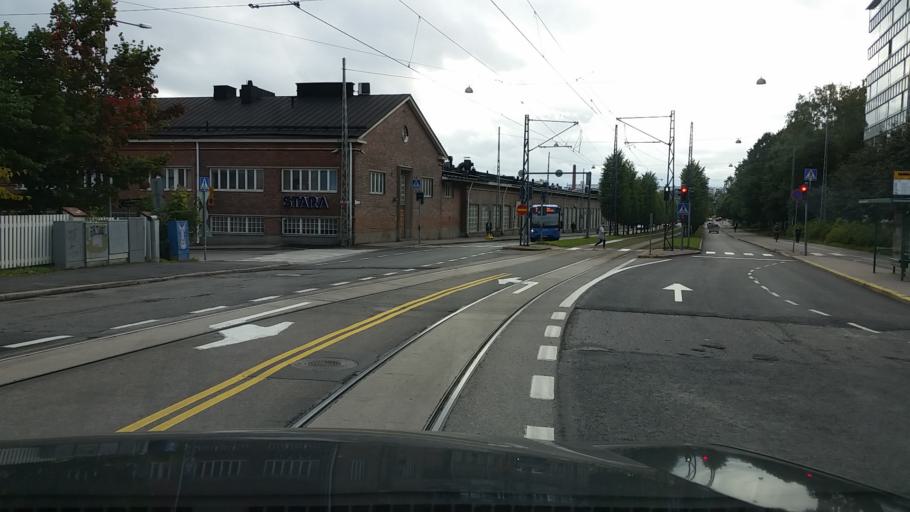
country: FI
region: Uusimaa
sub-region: Helsinki
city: Helsinki
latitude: 60.2061
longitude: 24.9729
